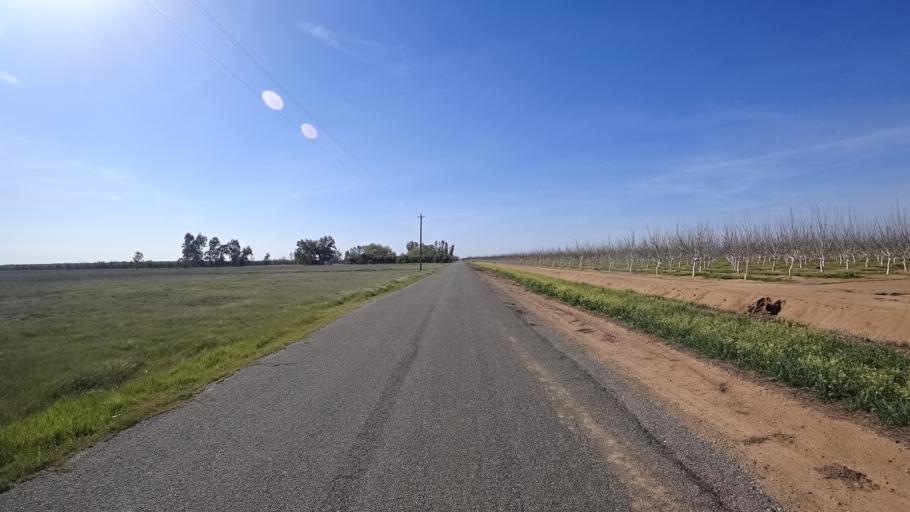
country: US
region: California
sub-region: Glenn County
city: Willows
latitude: 39.6208
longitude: -122.2130
